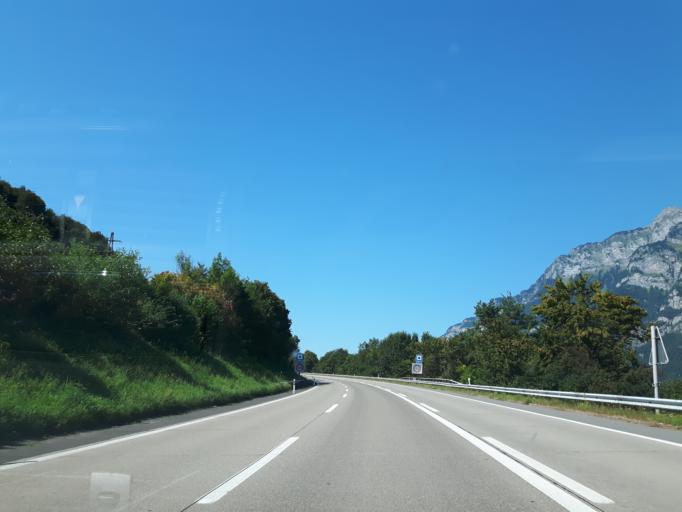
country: CH
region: Saint Gallen
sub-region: Wahlkreis Sarganserland
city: Quarten
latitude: 47.1133
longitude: 9.2658
